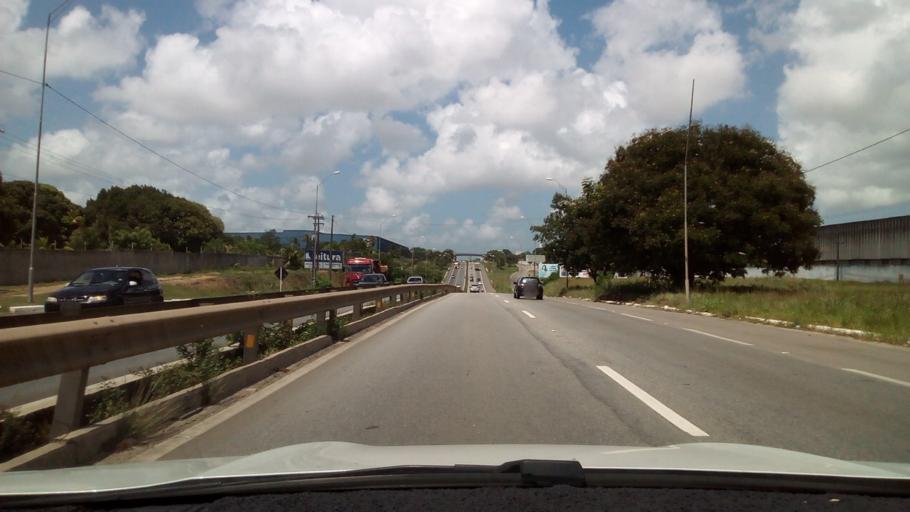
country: BR
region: Paraiba
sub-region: Bayeux
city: Bayeux
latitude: -7.1892
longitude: -34.9033
